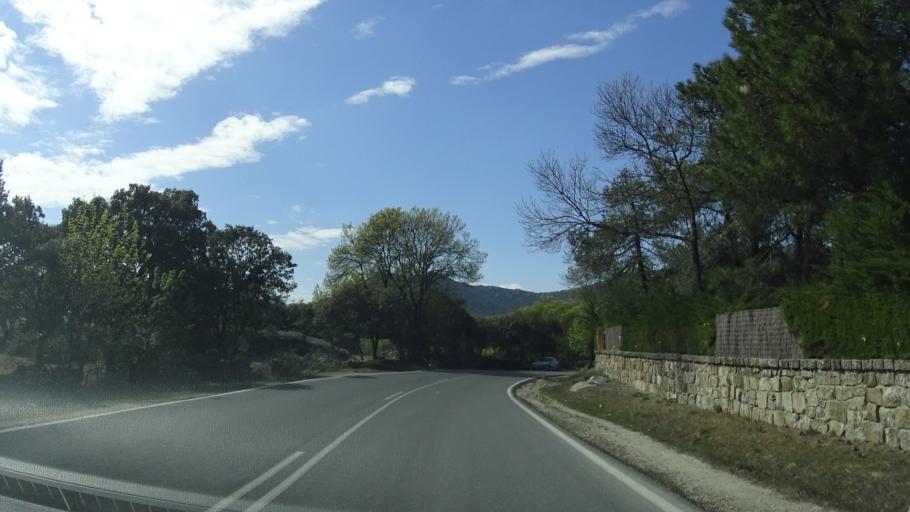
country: ES
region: Madrid
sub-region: Provincia de Madrid
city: Hoyo de Manzanares
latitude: 40.6224
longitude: -3.8952
